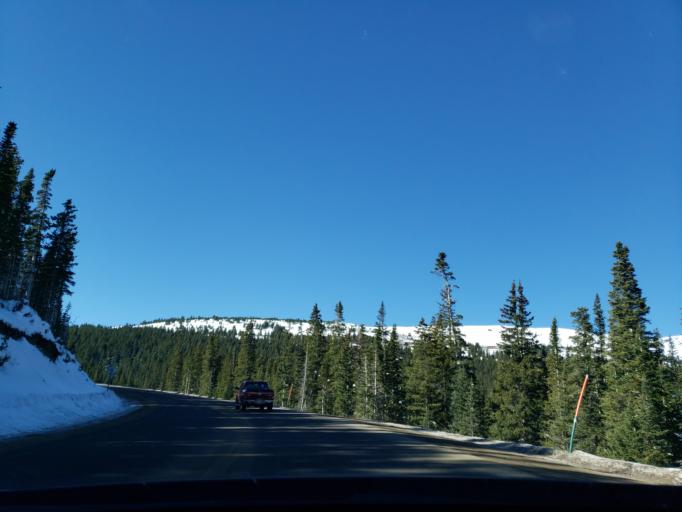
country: US
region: Colorado
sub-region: Summit County
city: Breckenridge
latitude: 39.3692
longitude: -106.0591
